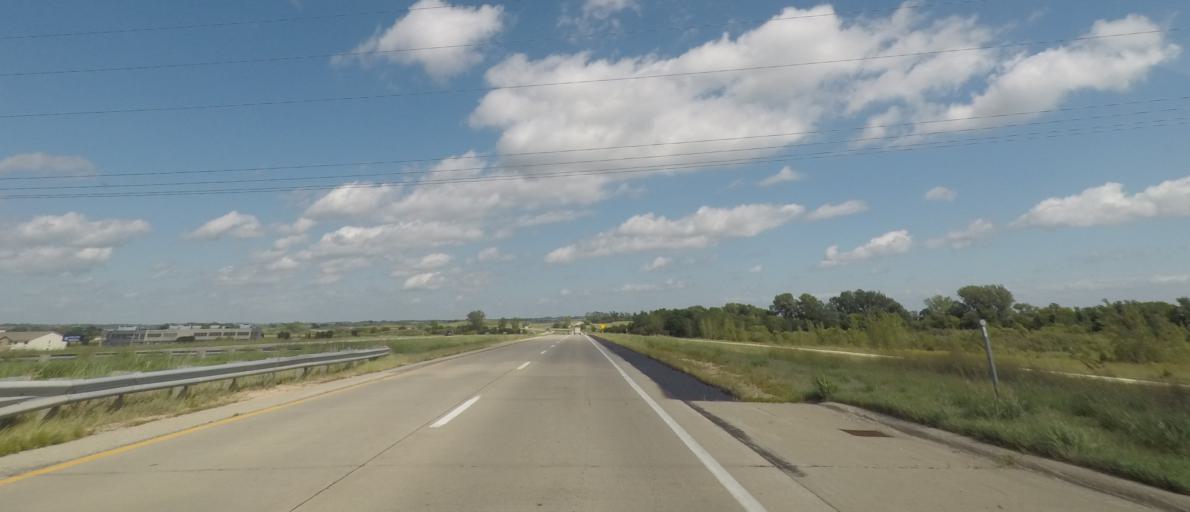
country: US
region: Iowa
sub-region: Jones County
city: Monticello
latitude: 42.2072
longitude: -91.1891
